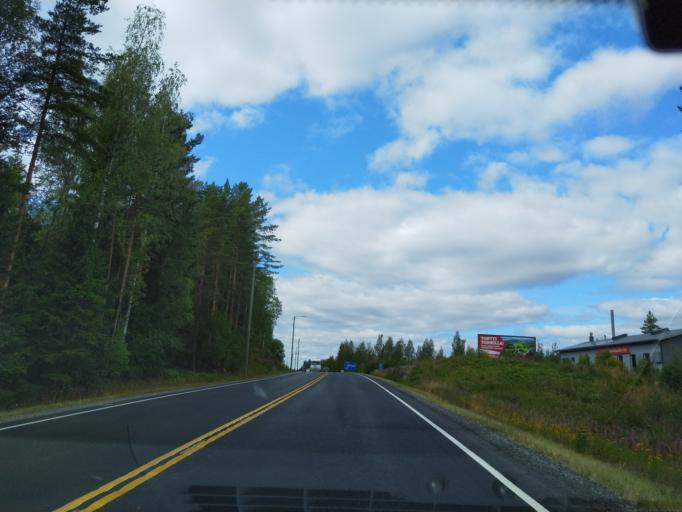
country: FI
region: Haeme
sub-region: Riihimaeki
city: Loppi
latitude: 60.7210
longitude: 24.4529
